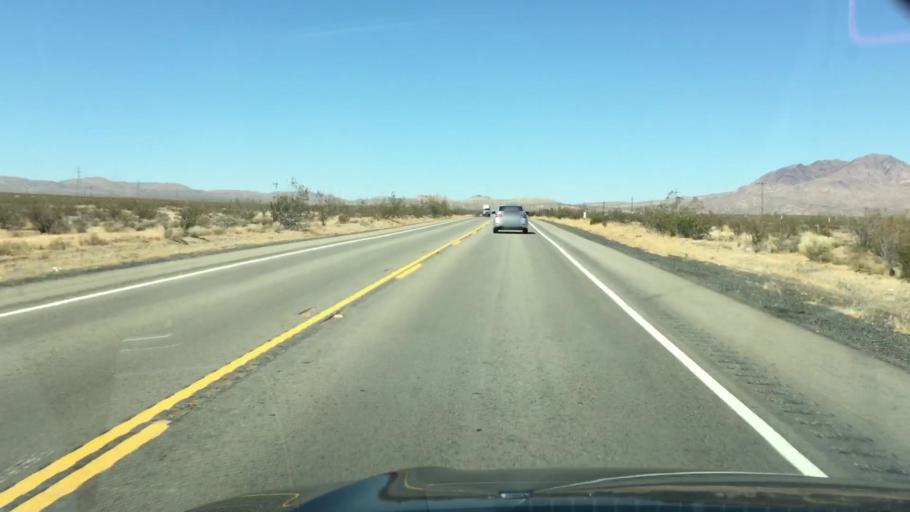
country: US
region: California
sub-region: Kern County
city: Boron
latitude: 35.2632
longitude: -117.6134
